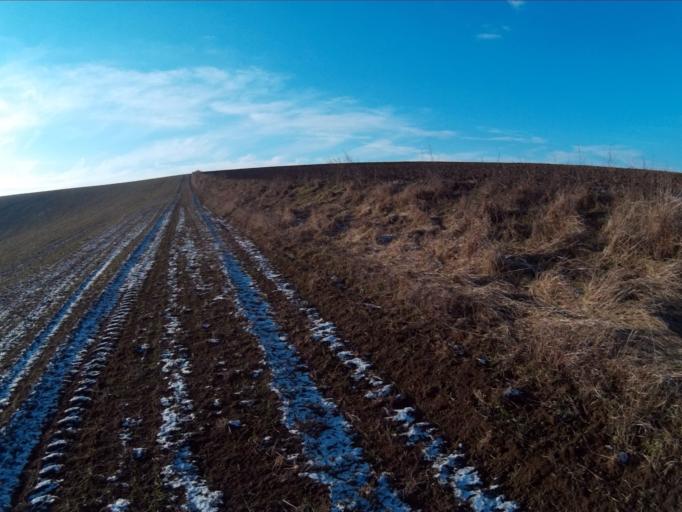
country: CZ
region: South Moravian
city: Krenovice
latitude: 49.1620
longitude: 16.8139
